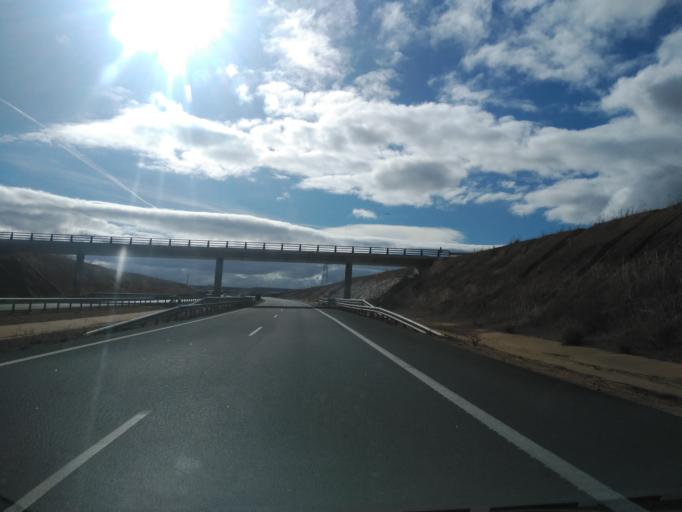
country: ES
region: Castille and Leon
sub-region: Provincia de Palencia
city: Marcilla de Campos
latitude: 42.3637
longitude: -4.3906
